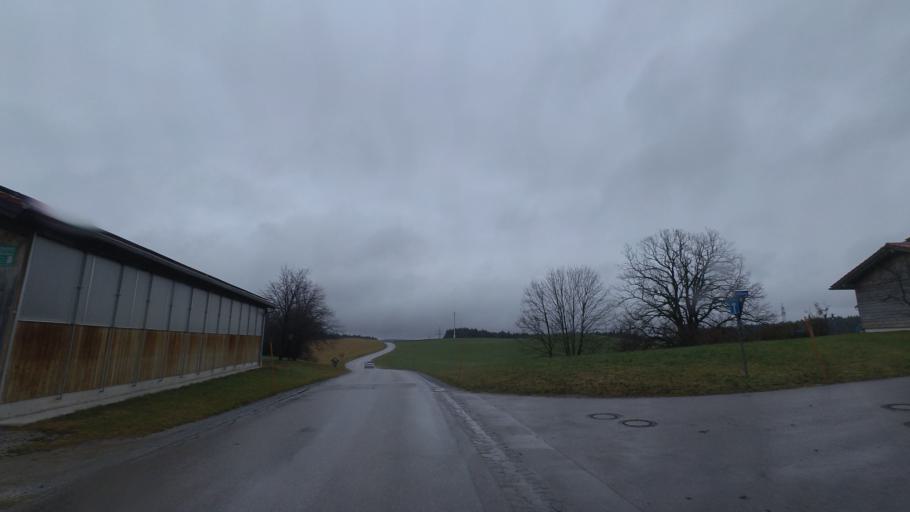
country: DE
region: Bavaria
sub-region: Upper Bavaria
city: Nussdorf
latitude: 47.9062
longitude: 12.5978
